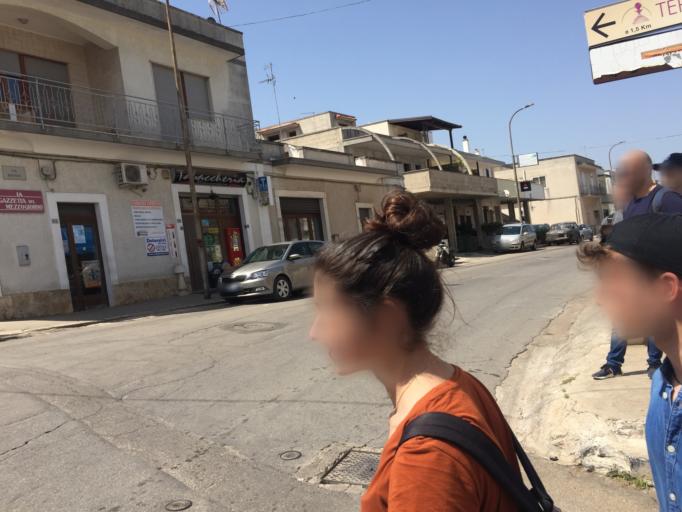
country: IT
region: Apulia
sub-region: Provincia di Brindisi
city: Casalini
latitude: 40.7381
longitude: 17.4715
